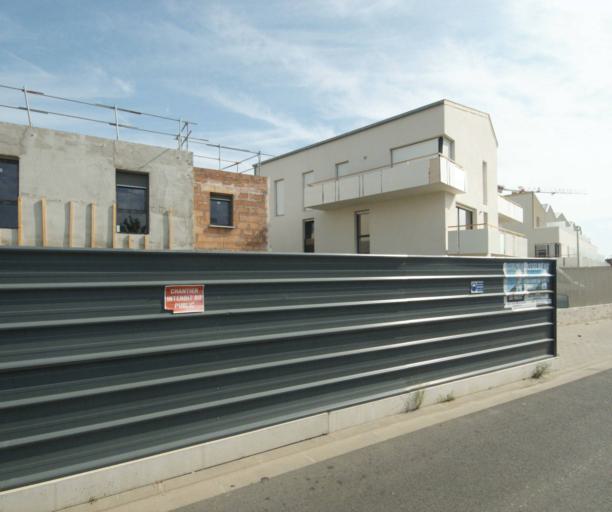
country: FR
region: Nord-Pas-de-Calais
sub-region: Departement du Nord
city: Lille
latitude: 50.6108
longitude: 3.0577
